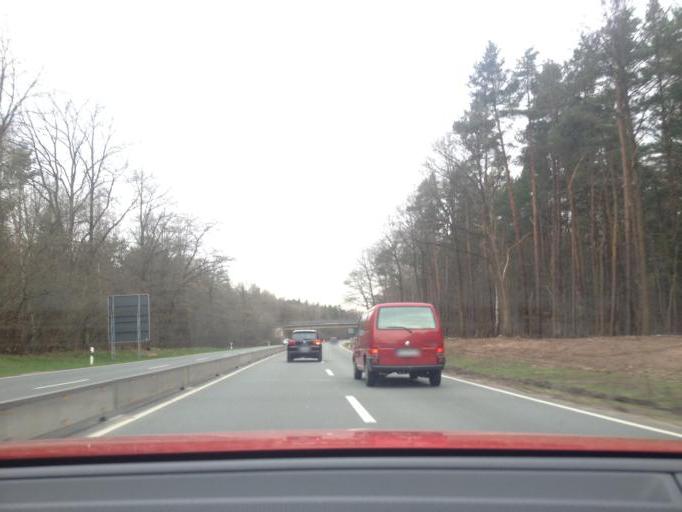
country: DE
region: Bavaria
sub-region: Regierungsbezirk Mittelfranken
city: Feucht
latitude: 49.4077
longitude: 11.1884
